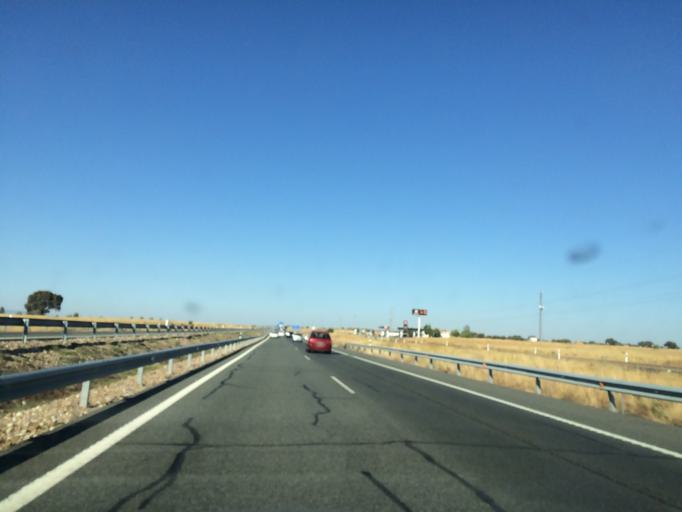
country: ES
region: Castille-La Mancha
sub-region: Province of Toledo
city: Calera y Chozas
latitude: 39.9268
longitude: -5.0219
